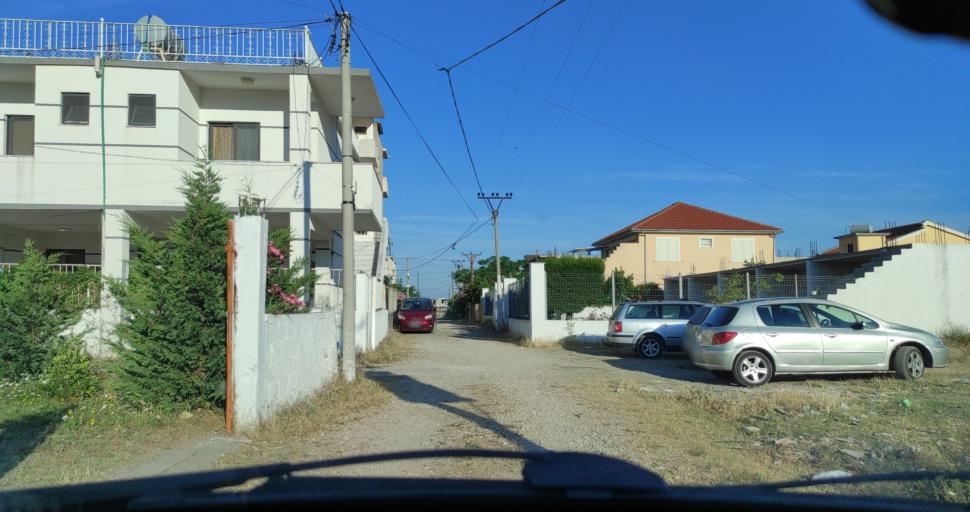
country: AL
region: Shkoder
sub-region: Rrethi i Shkodres
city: Velipoje
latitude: 41.8666
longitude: 19.4388
